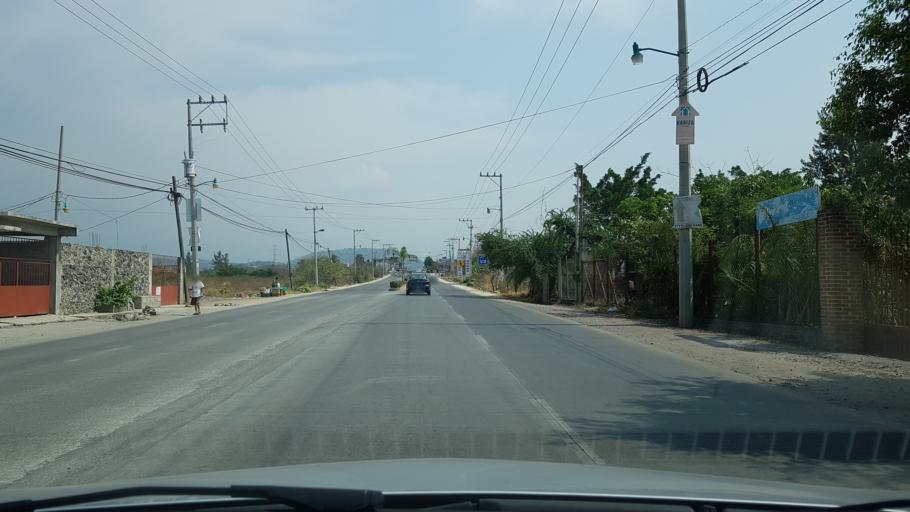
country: MX
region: Morelos
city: Emiliano Zapata
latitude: 18.8145
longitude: -99.1922
